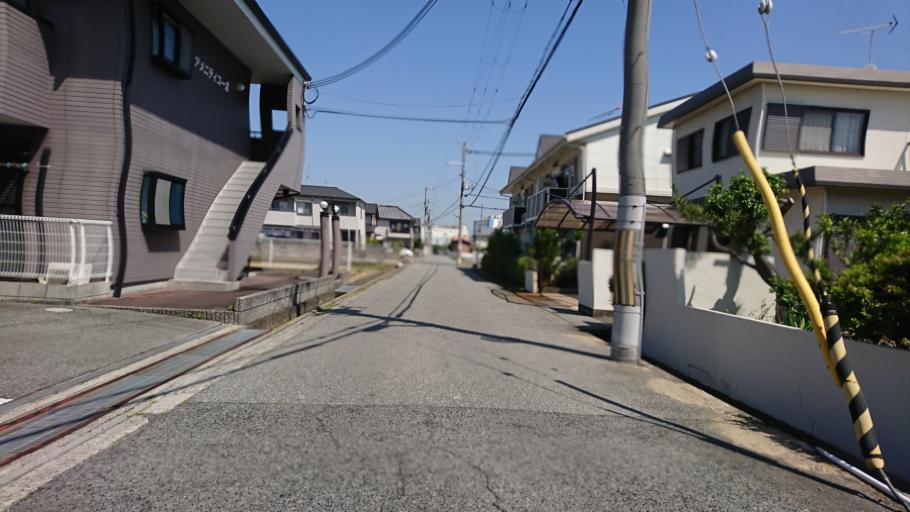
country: JP
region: Hyogo
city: Kakogawacho-honmachi
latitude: 34.7535
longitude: 134.8667
